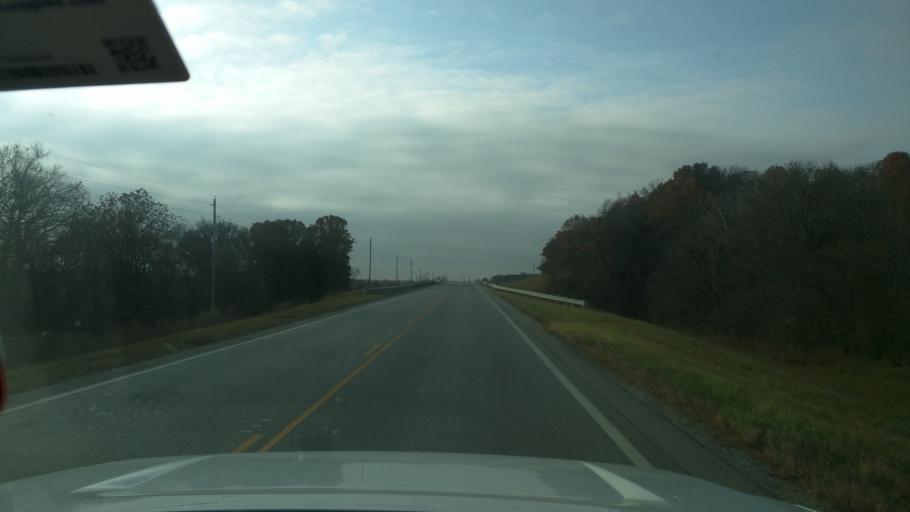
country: US
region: Kansas
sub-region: Greenwood County
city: Eureka
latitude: 37.7403
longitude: -96.2296
